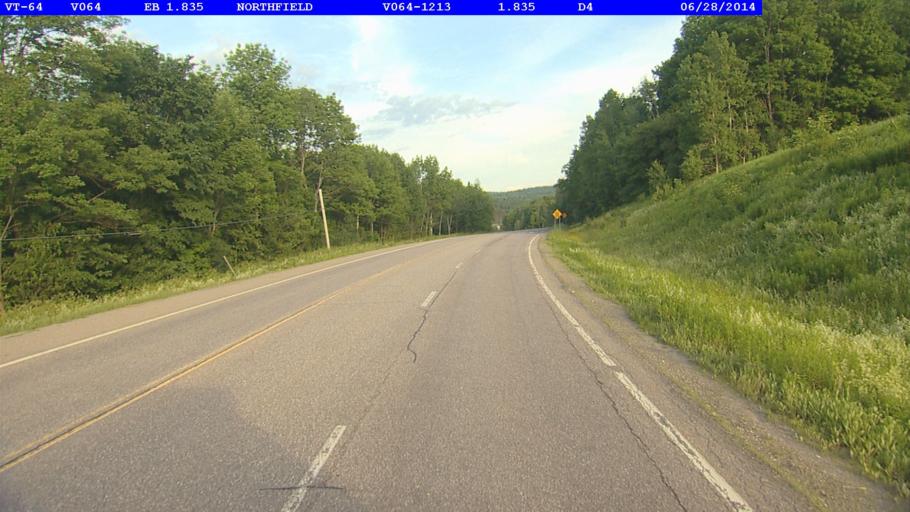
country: US
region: Vermont
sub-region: Washington County
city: Northfield
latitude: 44.1168
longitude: -72.6258
